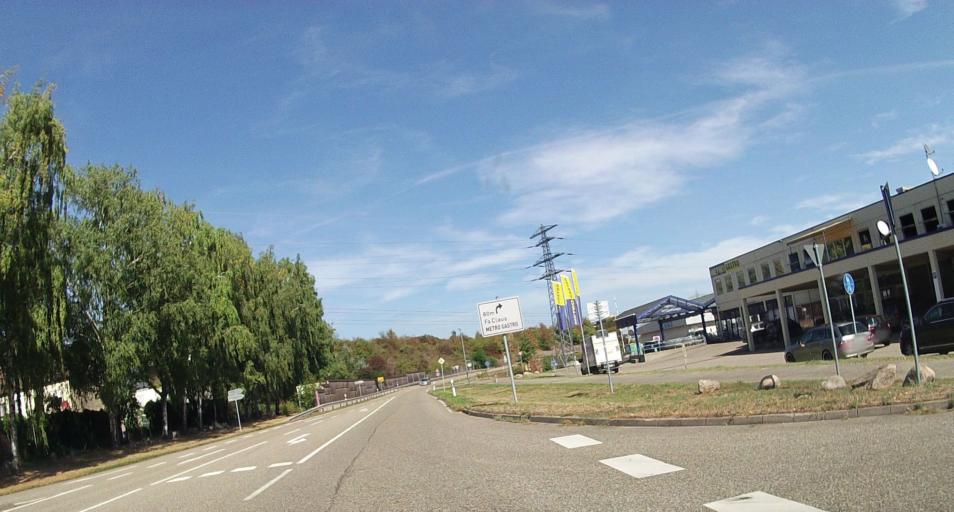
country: DE
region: Baden-Wuerttemberg
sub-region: Karlsruhe Region
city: Rastatt
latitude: 48.8153
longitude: 8.1957
